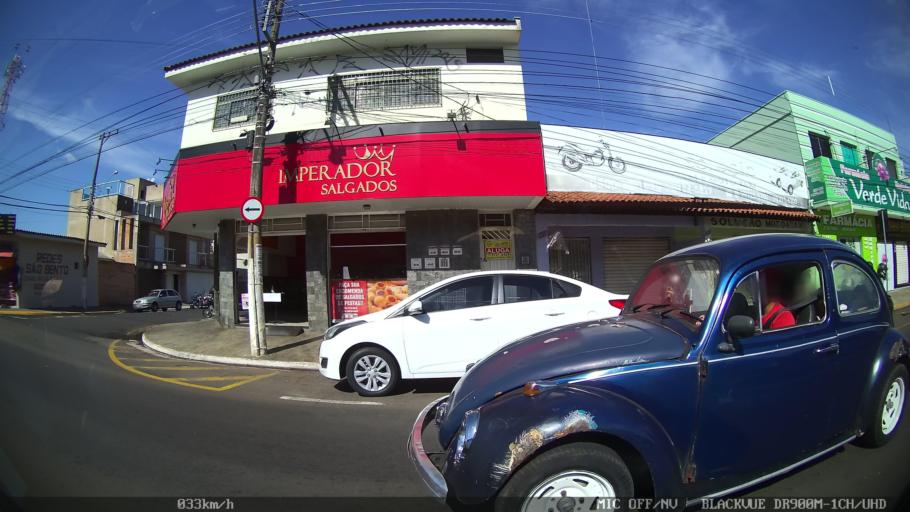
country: BR
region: Sao Paulo
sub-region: Franca
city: Franca
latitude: -20.5147
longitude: -47.4057
